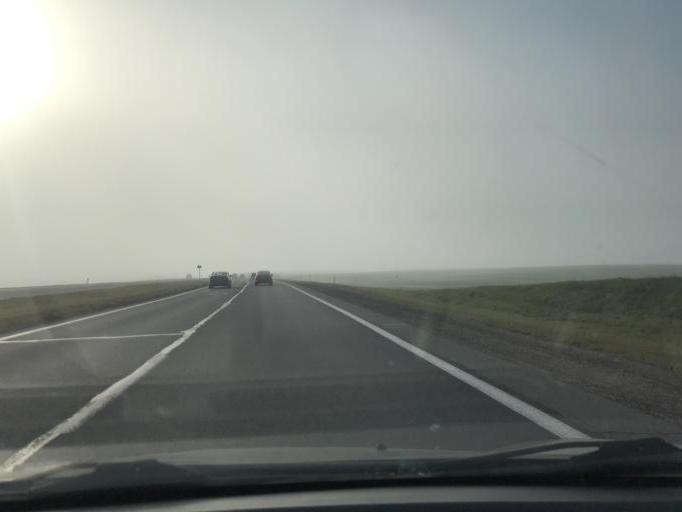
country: BY
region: Minsk
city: Luhavaya Slabada
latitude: 53.7515
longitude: 27.8325
